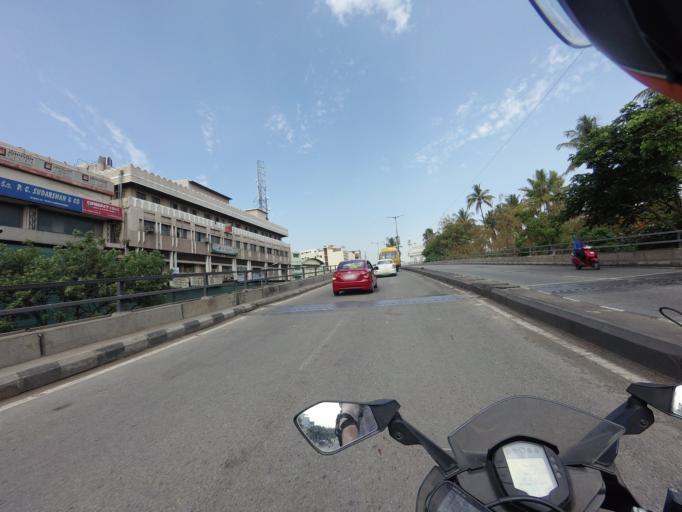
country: IN
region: Karnataka
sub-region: Bangalore Urban
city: Bangalore
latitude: 12.9636
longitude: 77.5798
